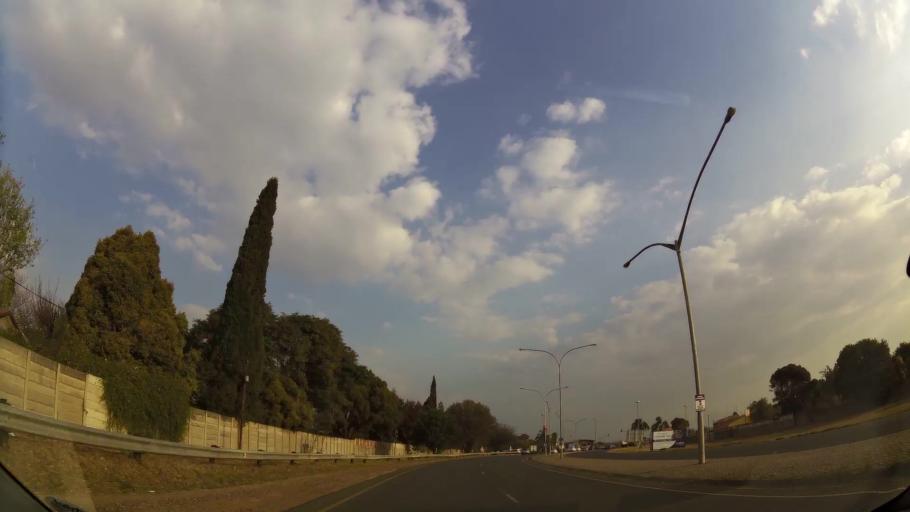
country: ZA
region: Gauteng
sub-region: Ekurhuleni Metropolitan Municipality
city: Benoni
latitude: -26.1344
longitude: 28.2936
